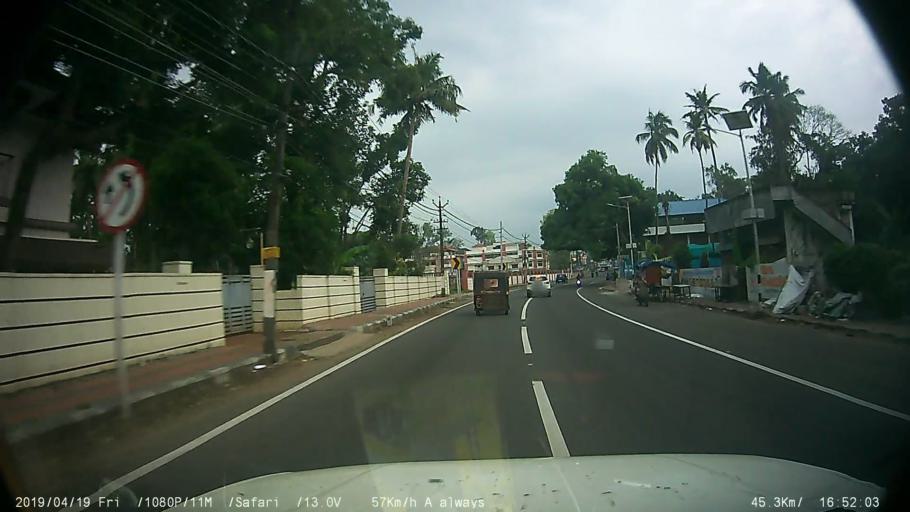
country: IN
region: Kerala
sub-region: Kottayam
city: Changanacheri
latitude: 9.4537
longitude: 76.5366
